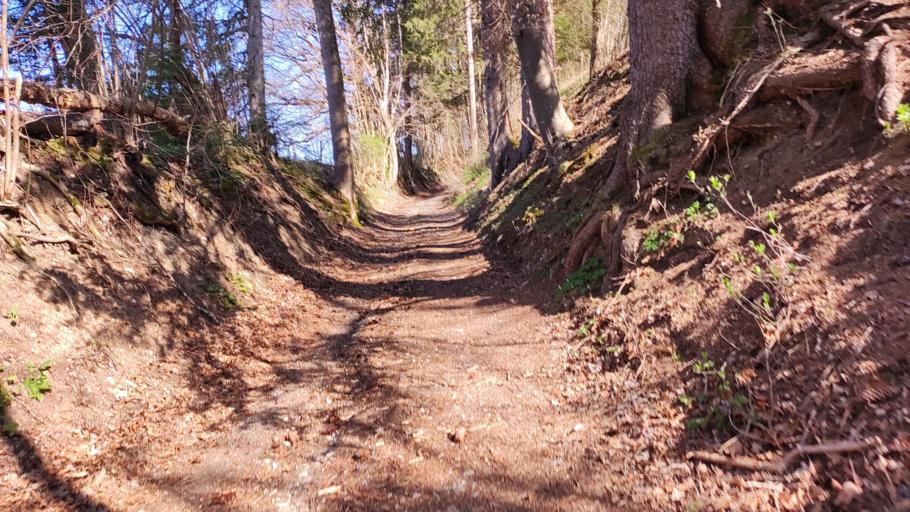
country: DE
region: Bavaria
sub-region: Upper Bavaria
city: Unterammergau
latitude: 47.6351
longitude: 11.0292
